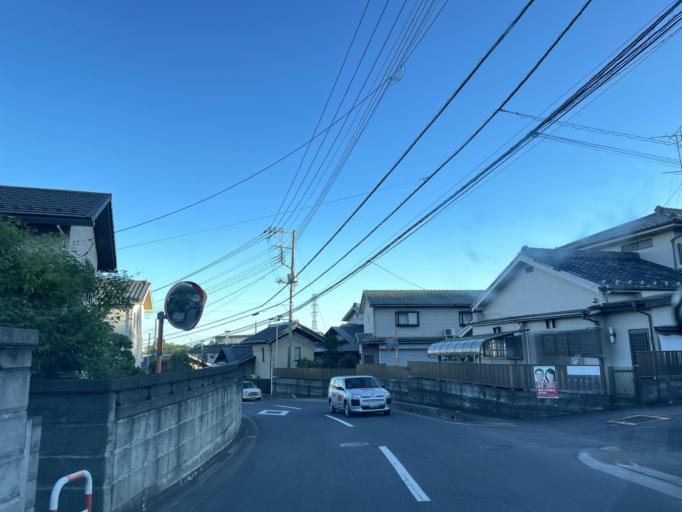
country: JP
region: Saitama
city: Hanno
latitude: 35.8254
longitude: 139.3627
